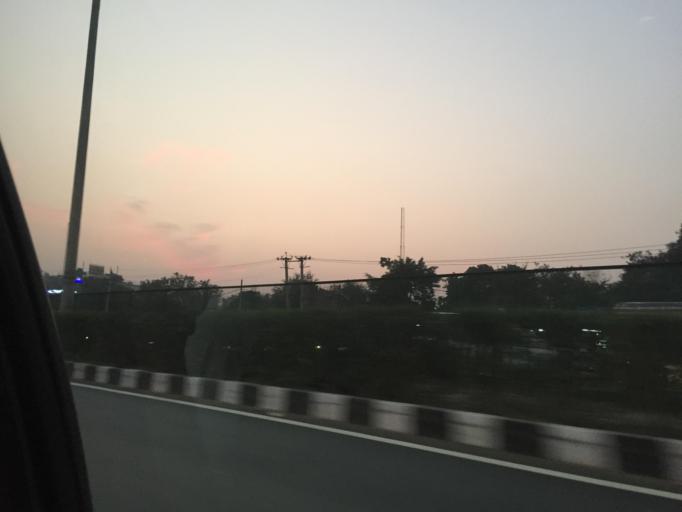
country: IN
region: Haryana
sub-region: Gurgaon
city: Gurgaon
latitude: 28.5181
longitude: 77.0960
